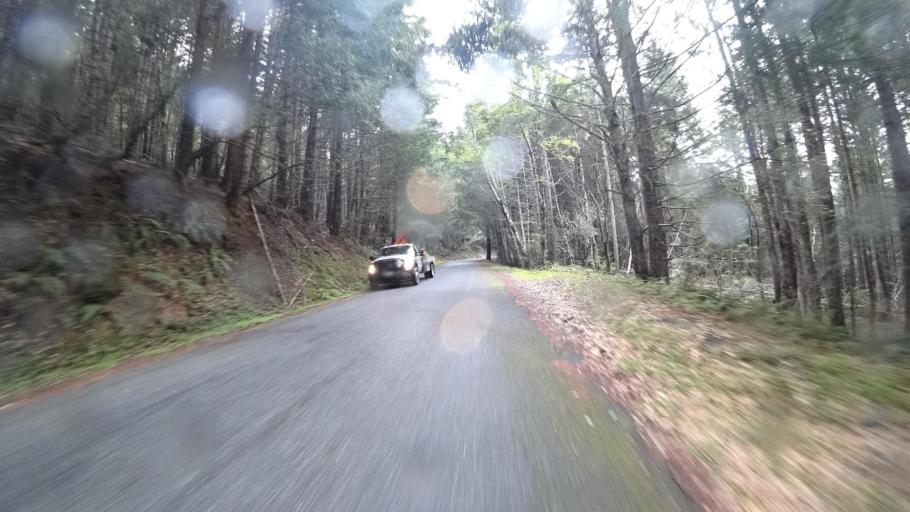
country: US
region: California
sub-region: Humboldt County
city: Willow Creek
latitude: 41.2025
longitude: -123.7818
